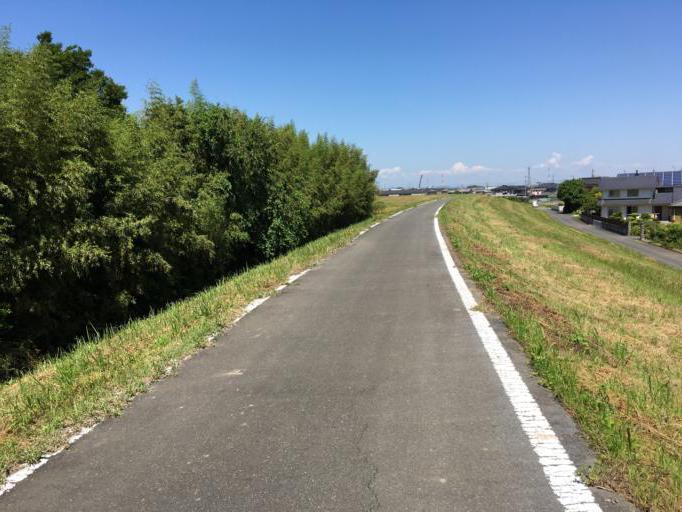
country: JP
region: Saitama
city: Kawagoe
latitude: 35.9605
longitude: 139.4788
